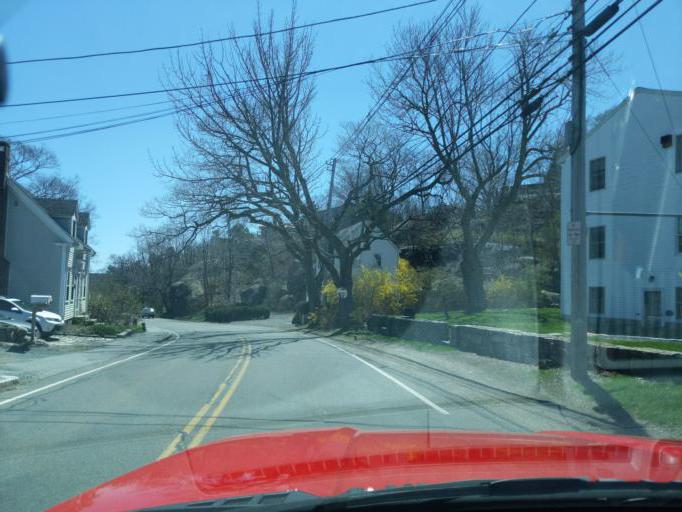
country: US
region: Massachusetts
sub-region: Essex County
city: Rockport
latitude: 42.6666
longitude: -70.6253
